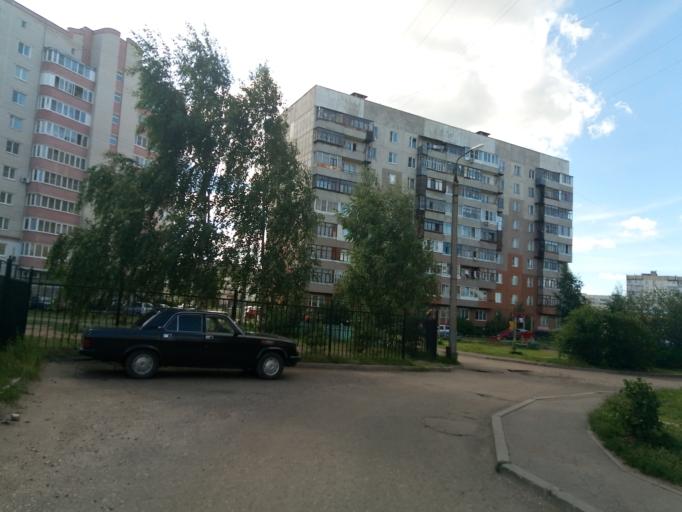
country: RU
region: Jaroslavl
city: Yaroslavl
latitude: 57.6393
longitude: 39.9502
